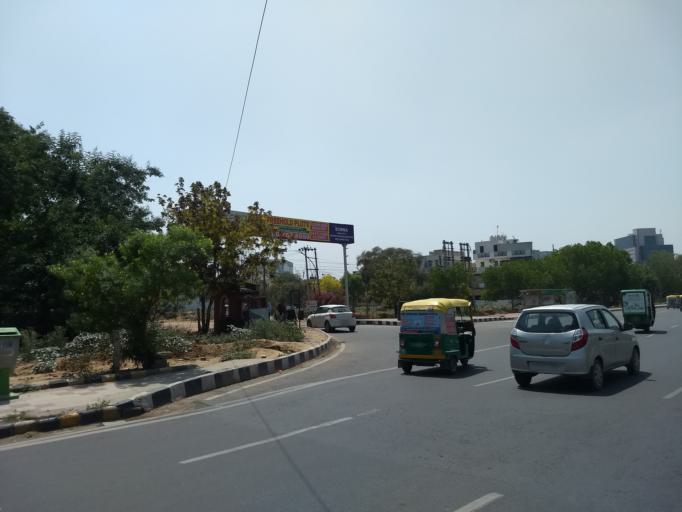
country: IN
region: Haryana
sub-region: Gurgaon
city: Gurgaon
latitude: 28.4639
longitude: 77.0641
